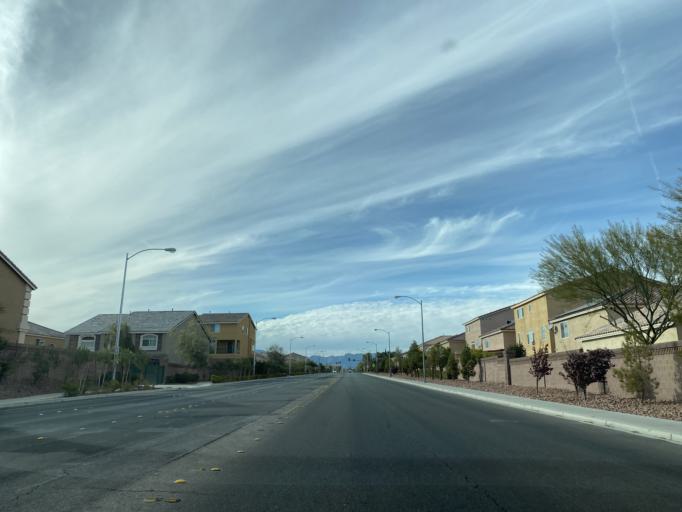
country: US
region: Nevada
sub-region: Clark County
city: Enterprise
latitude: 36.0347
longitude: -115.2310
